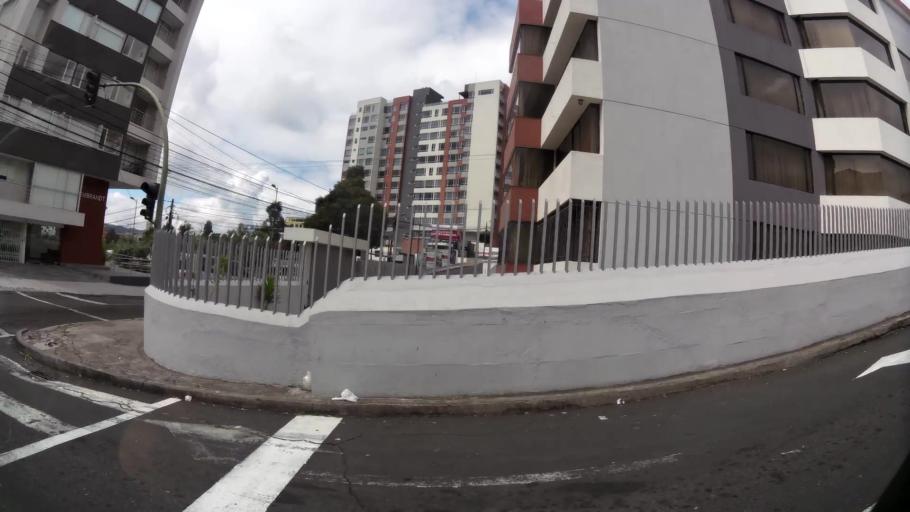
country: EC
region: Pichincha
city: Quito
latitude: -0.1632
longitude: -78.4964
